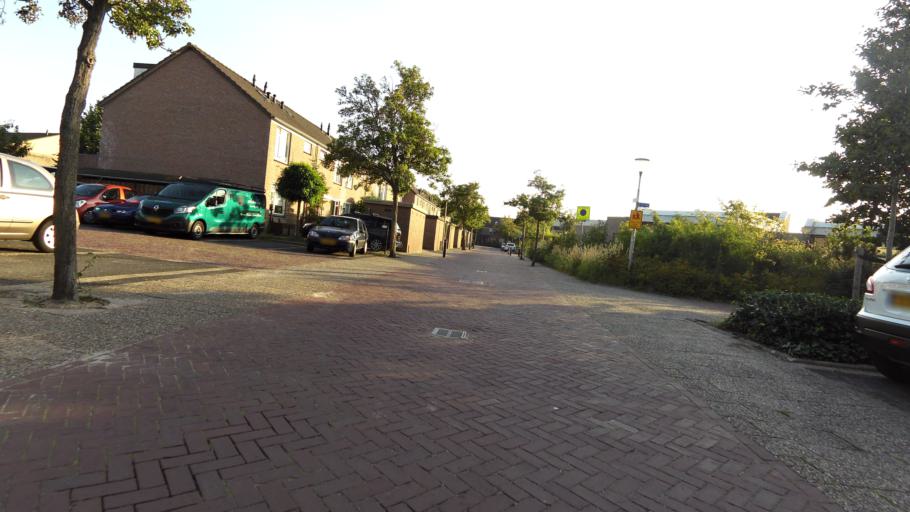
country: NL
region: South Holland
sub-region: Gemeente Teylingen
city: Sassenheim
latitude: 52.2227
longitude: 4.5120
